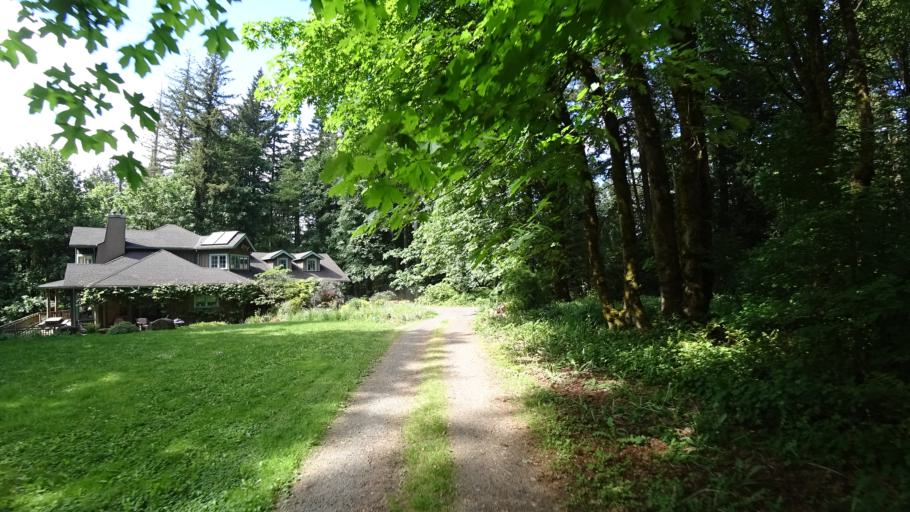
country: US
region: Oregon
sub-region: Washington County
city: Cedar Mill
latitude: 45.5782
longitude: -122.7927
